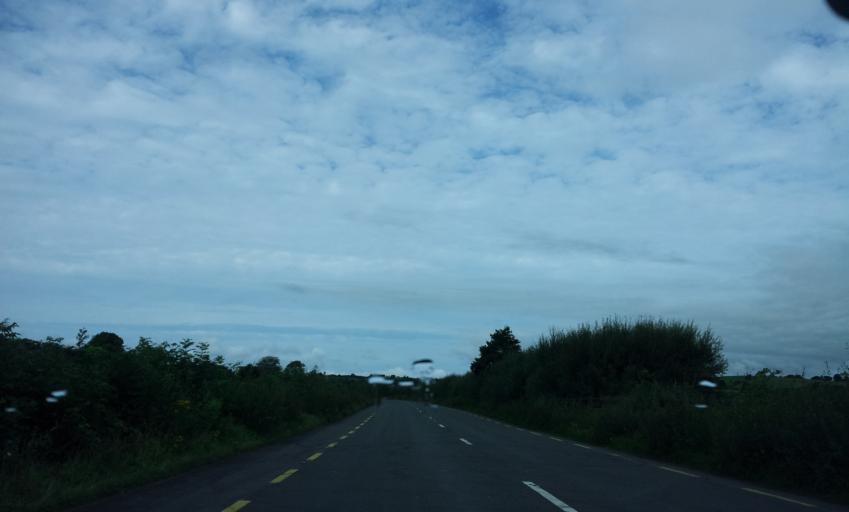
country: IE
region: Munster
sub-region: Ciarrai
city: Cill Airne
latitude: 52.0732
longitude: -9.6156
